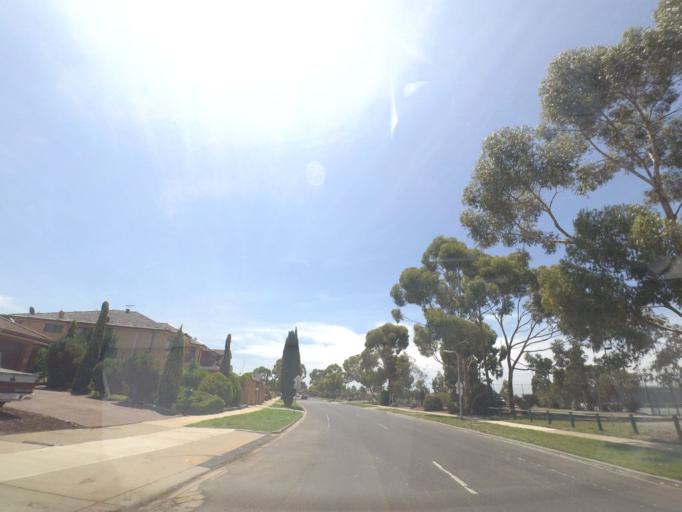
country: AU
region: Victoria
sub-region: Brimbank
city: Taylors Lakes
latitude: -37.7092
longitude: 144.7910
